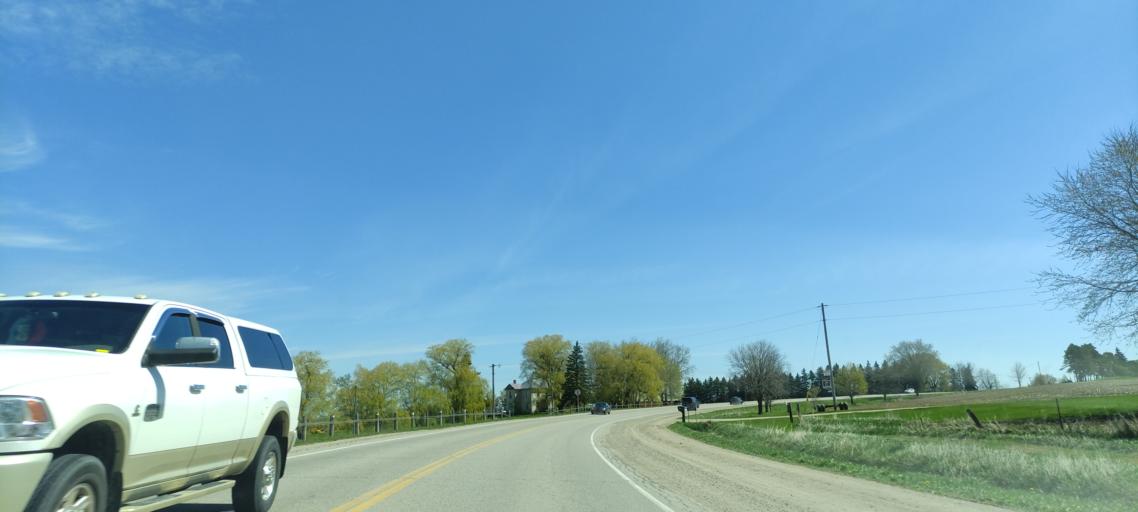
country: CA
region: Ontario
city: Waterloo
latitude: 43.6029
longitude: -80.6034
